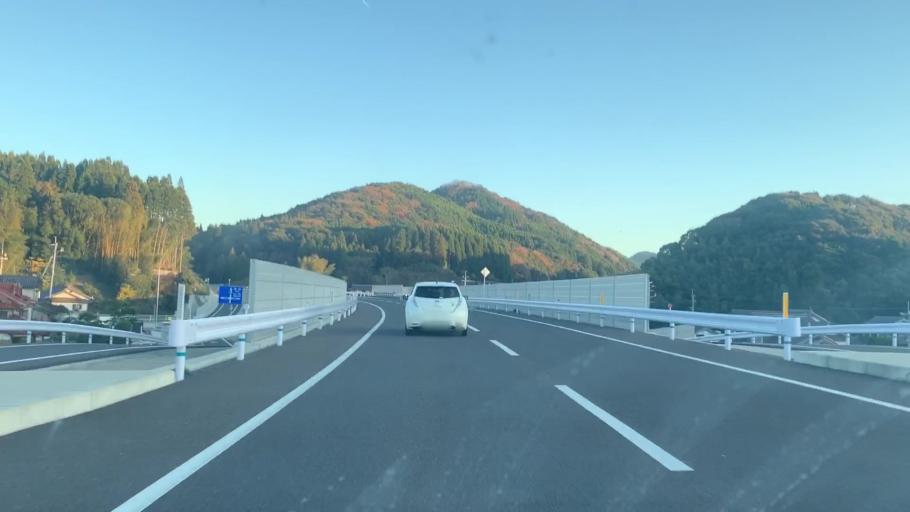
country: JP
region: Saga Prefecture
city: Takeocho-takeo
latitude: 33.2586
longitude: 129.9741
